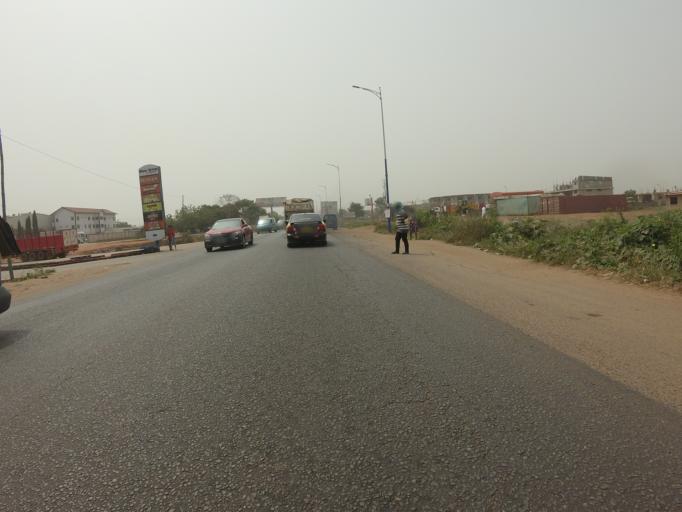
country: GH
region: Greater Accra
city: Tema
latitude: 5.7187
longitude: 0.0169
